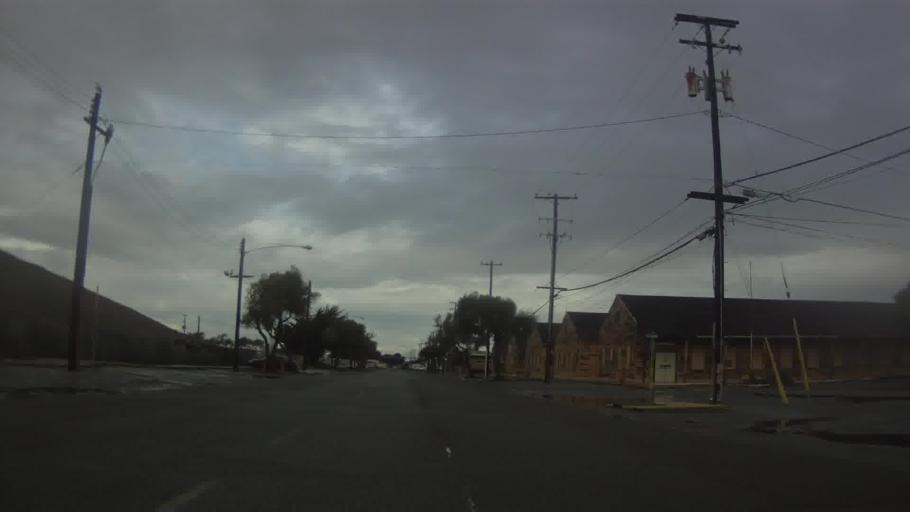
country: US
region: California
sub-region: San Francisco County
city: San Francisco
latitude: 37.8236
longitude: -122.3689
